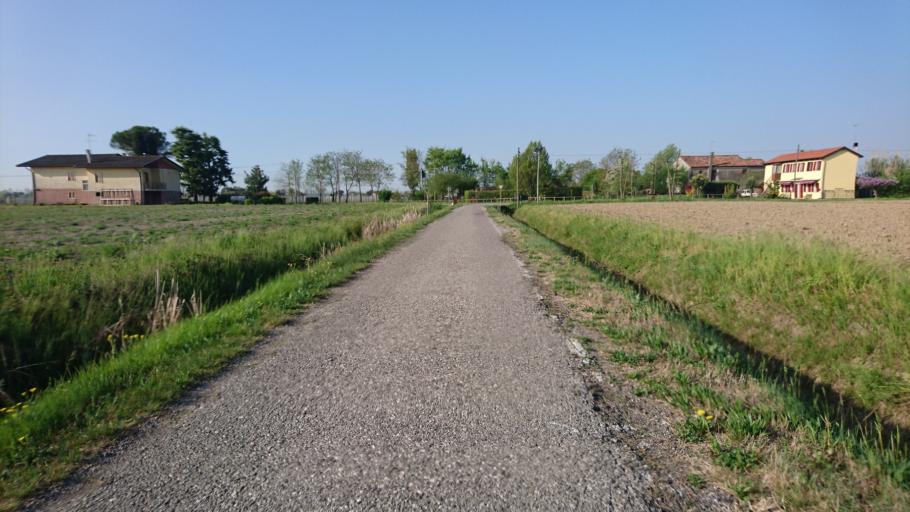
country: IT
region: Veneto
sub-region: Provincia di Venezia
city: Fossalta di Piave
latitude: 45.6555
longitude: 12.5020
